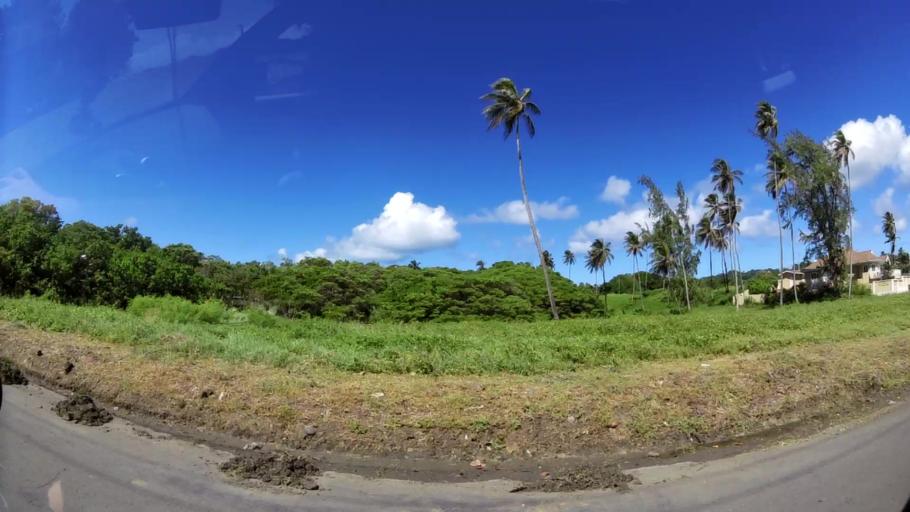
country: TT
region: Tobago
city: Scarborough
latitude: 11.1629
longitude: -60.7663
